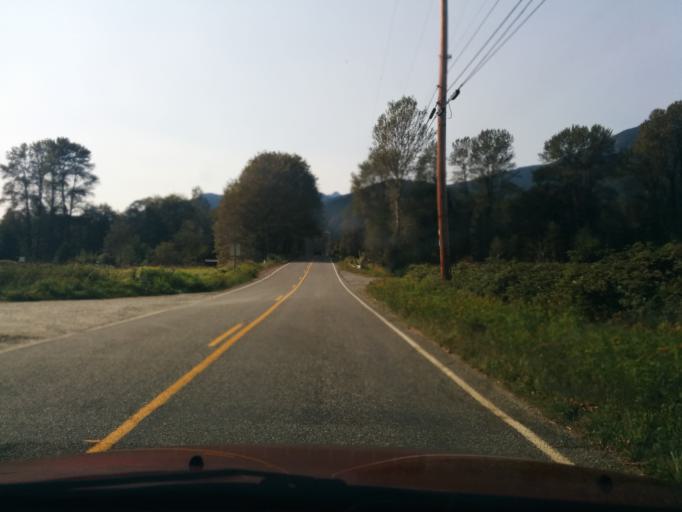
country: US
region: Washington
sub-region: Snohomish County
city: Darrington
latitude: 48.5267
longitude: -121.4258
